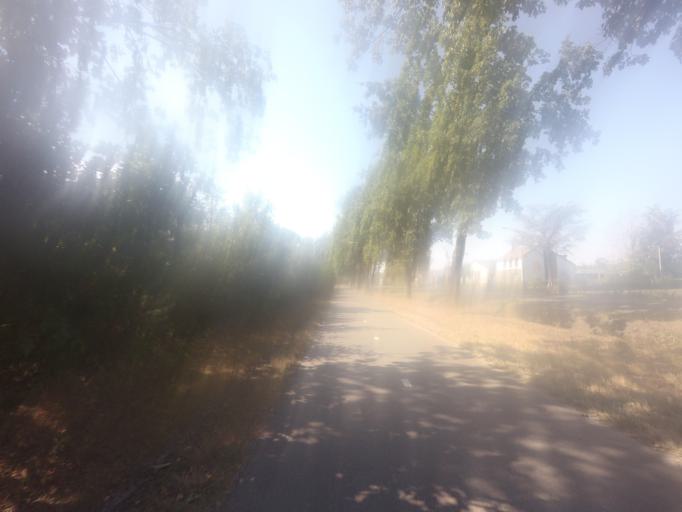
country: NL
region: North Brabant
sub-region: Gemeente Goirle
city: Goirle
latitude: 51.5100
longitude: 5.0953
